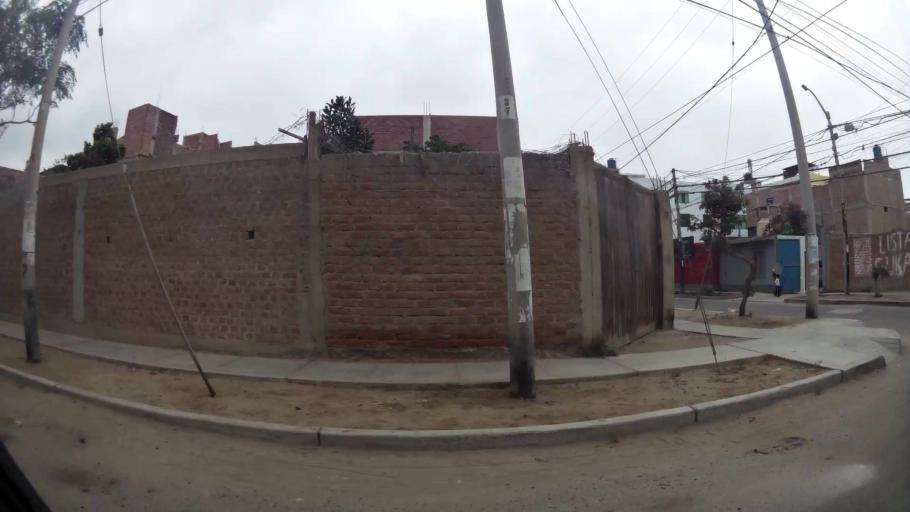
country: PE
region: La Libertad
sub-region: Provincia de Trujillo
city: Trujillo
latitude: -8.1095
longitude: -79.0433
